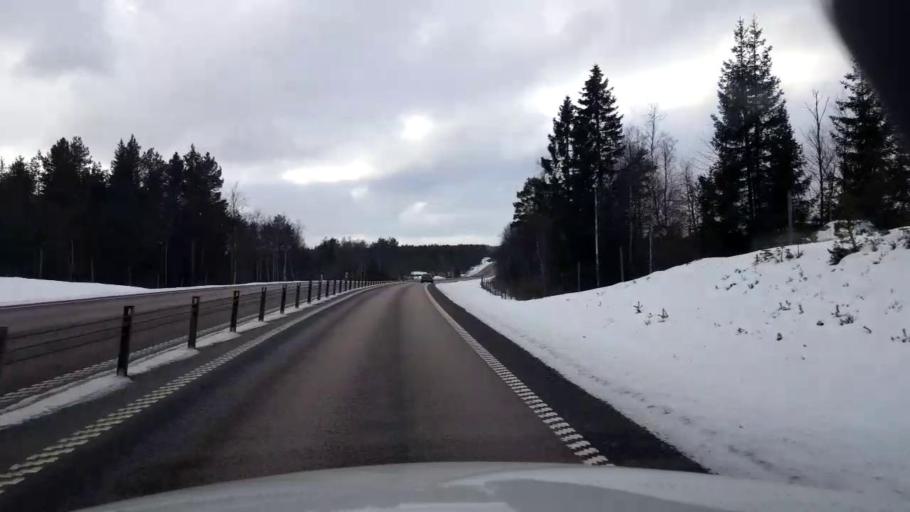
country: SE
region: Gaevleborg
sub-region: Hudiksvalls Kommun
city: Hudiksvall
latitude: 61.8109
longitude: 17.1872
